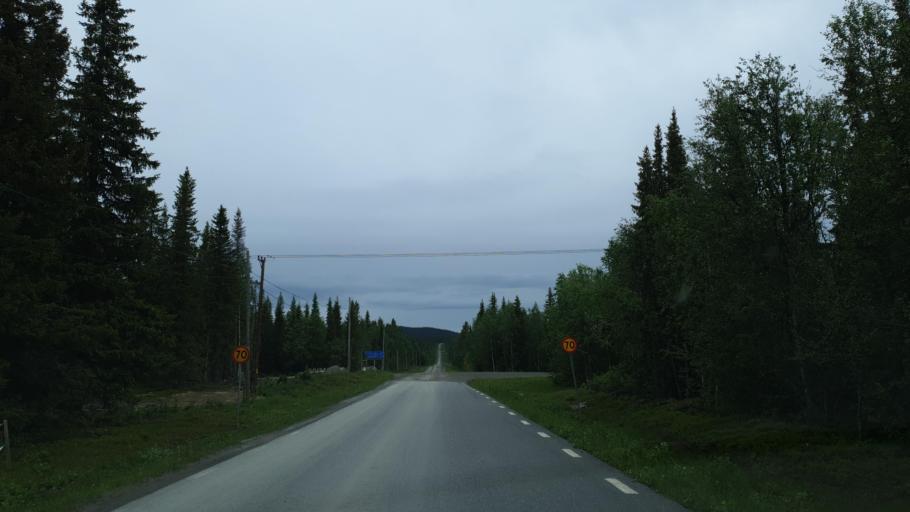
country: SE
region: Vaesterbotten
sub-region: Vilhelmina Kommun
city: Sjoberg
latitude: 65.3520
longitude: 16.1316
